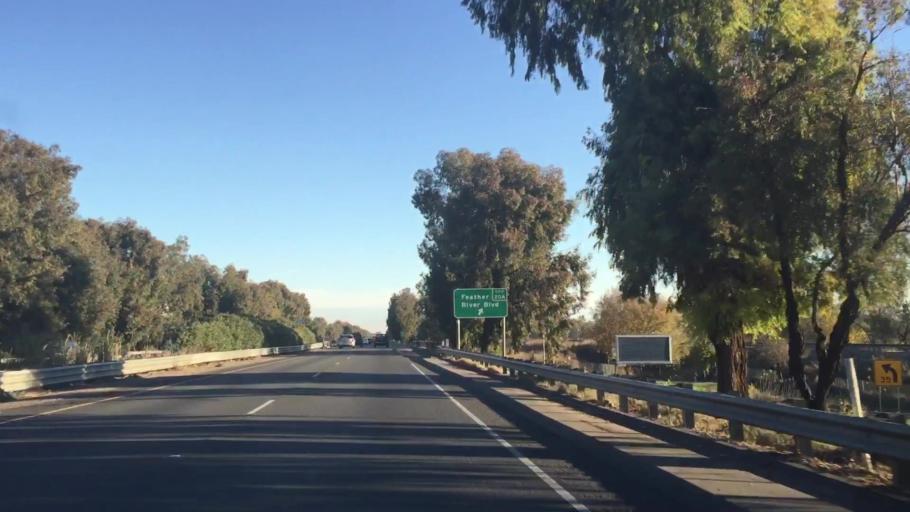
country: US
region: California
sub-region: Yuba County
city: Marysville
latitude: 39.1270
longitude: -121.5814
